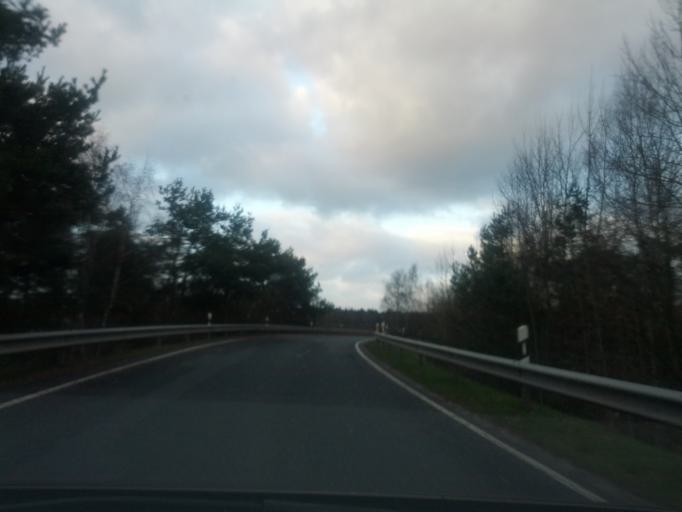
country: DE
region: Lower Saxony
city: Rotenburg
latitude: 53.1203
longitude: 9.3944
